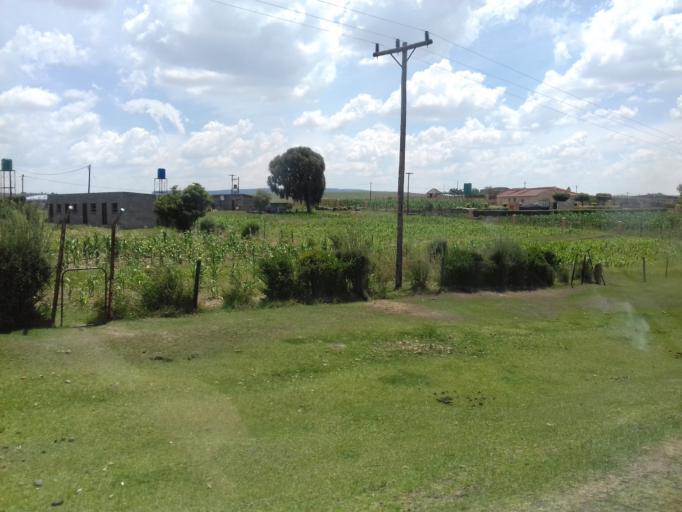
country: LS
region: Maseru
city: Nako
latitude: -29.5946
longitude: 27.5596
